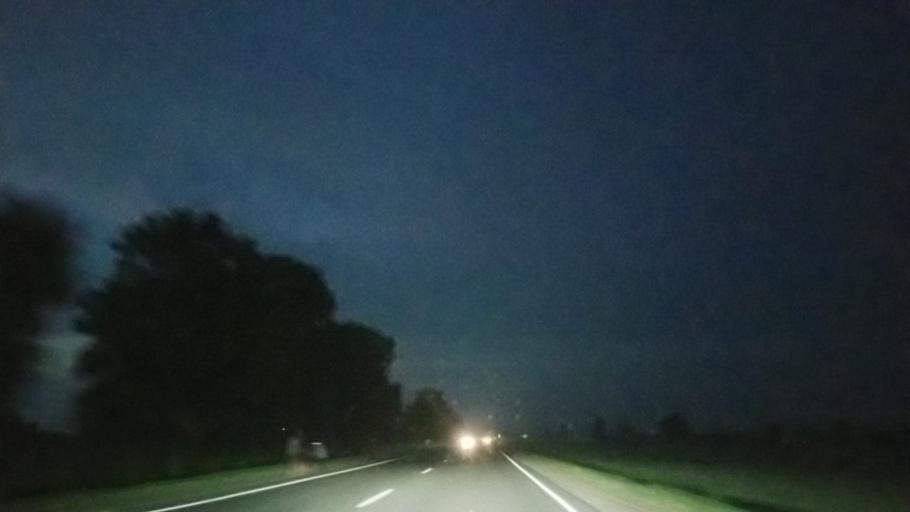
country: BY
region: Brest
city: Brest
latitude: 51.9884
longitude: 23.7048
